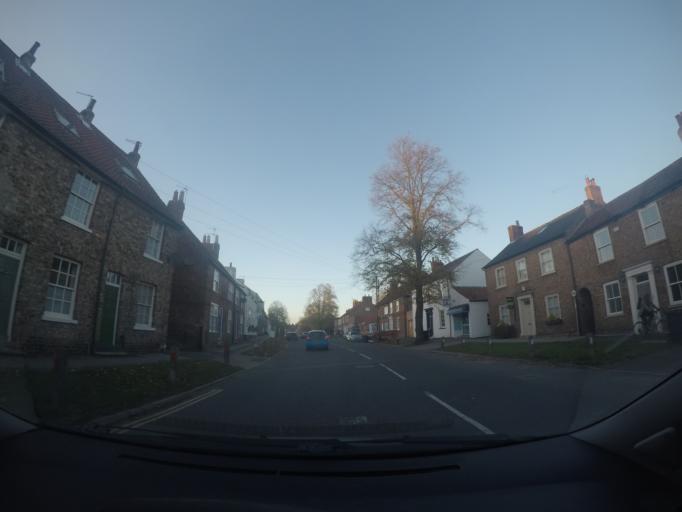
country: GB
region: England
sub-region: City of York
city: Fulford
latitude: 53.9347
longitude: -1.0714
